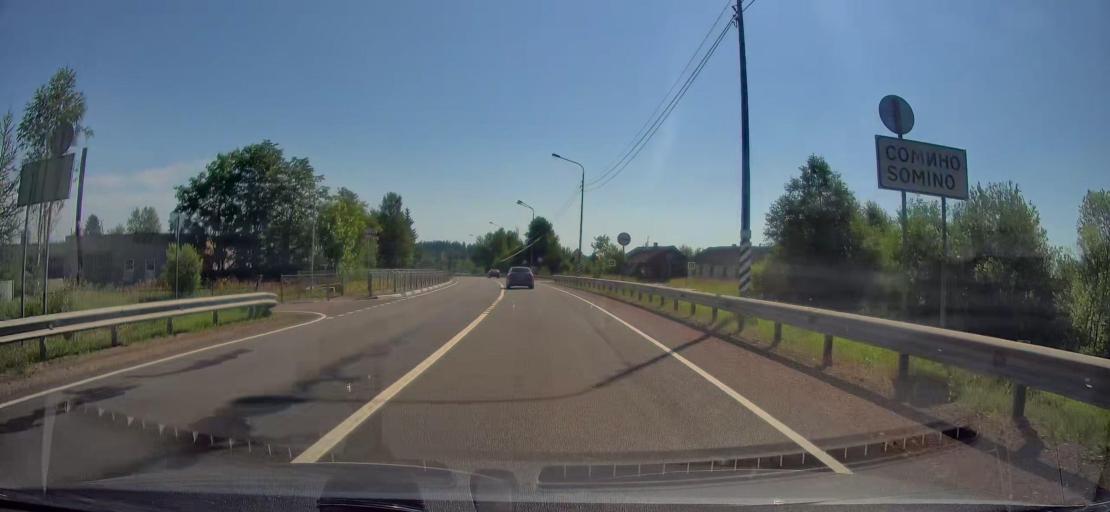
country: RU
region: Leningrad
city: Yefimovskiy
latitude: 59.3474
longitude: 34.8409
